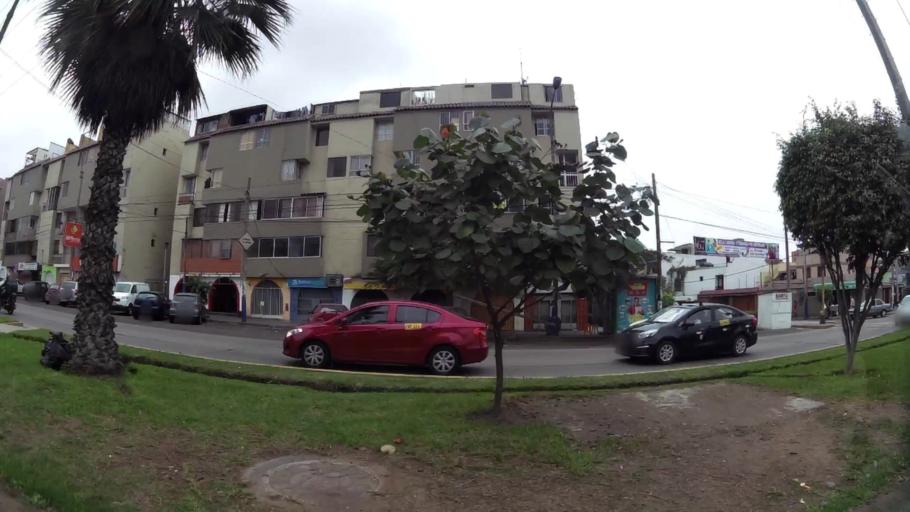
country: PE
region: Lima
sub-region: Lima
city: Surco
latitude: -12.1208
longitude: -77.0036
